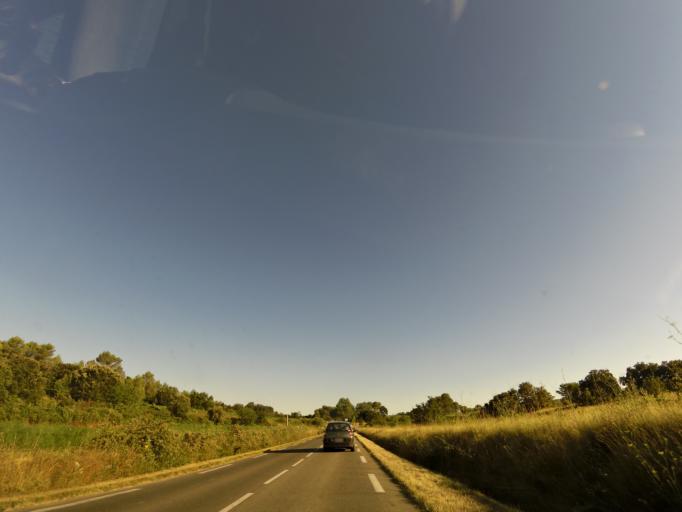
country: FR
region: Languedoc-Roussillon
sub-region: Departement du Gard
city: Sommieres
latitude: 43.8211
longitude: 4.0518
